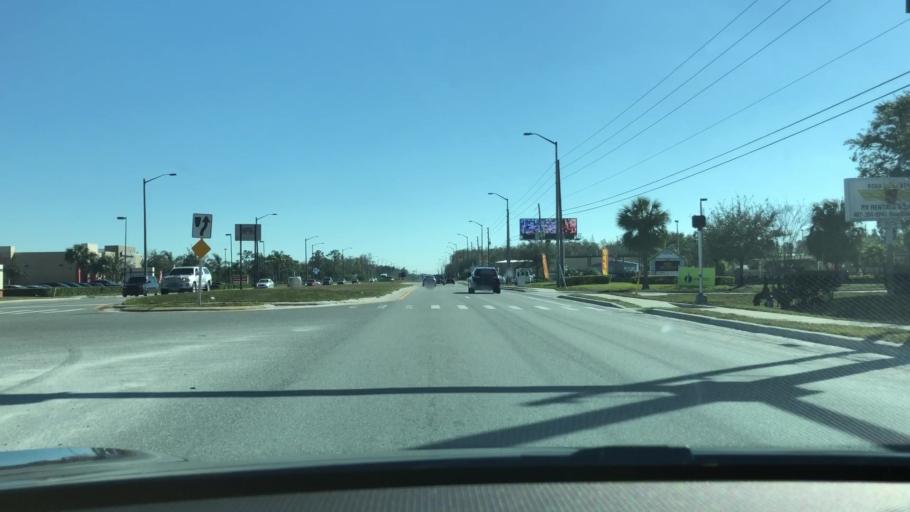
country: US
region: Florida
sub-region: Orange County
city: Conway
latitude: 28.4629
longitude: -81.2735
